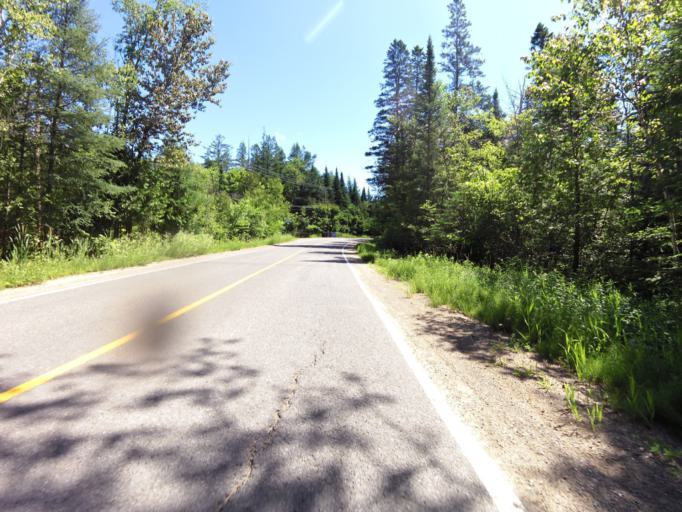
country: CA
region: Quebec
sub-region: Laurentides
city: Brownsburg-Chatham
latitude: 45.8469
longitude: -74.4644
